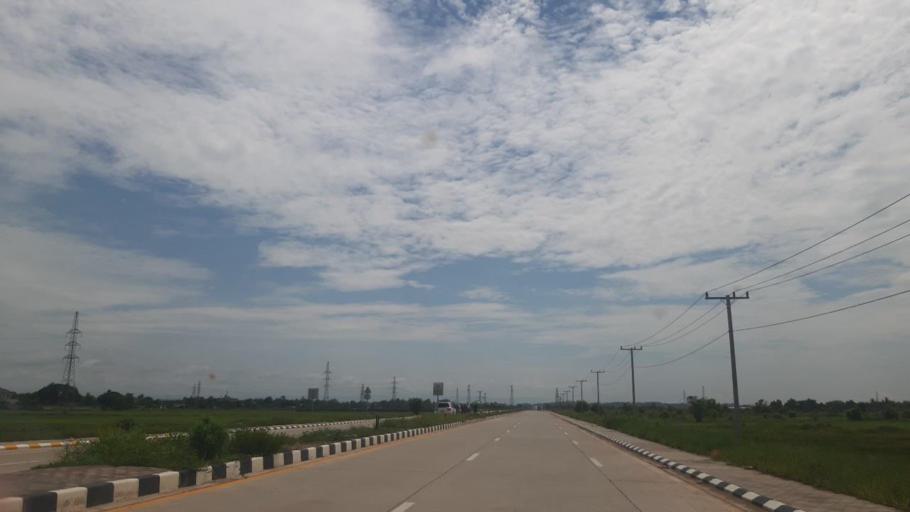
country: LA
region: Vientiane
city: Vientiane
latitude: 18.0187
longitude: 102.5918
